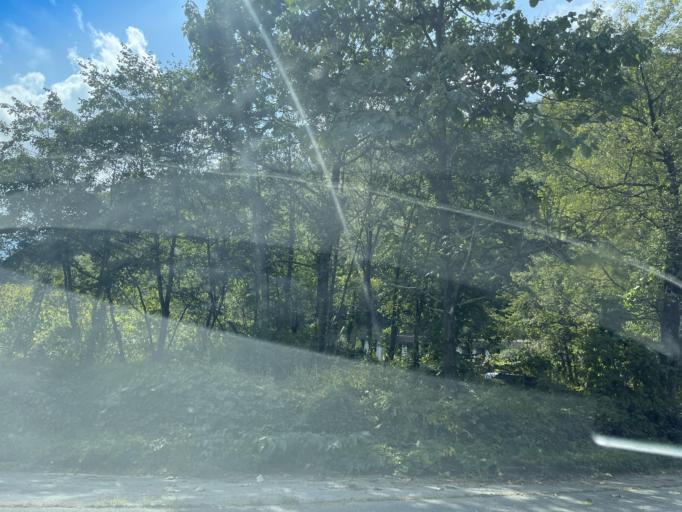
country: JP
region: Nagano
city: Omachi
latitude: 36.5264
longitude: 137.7907
